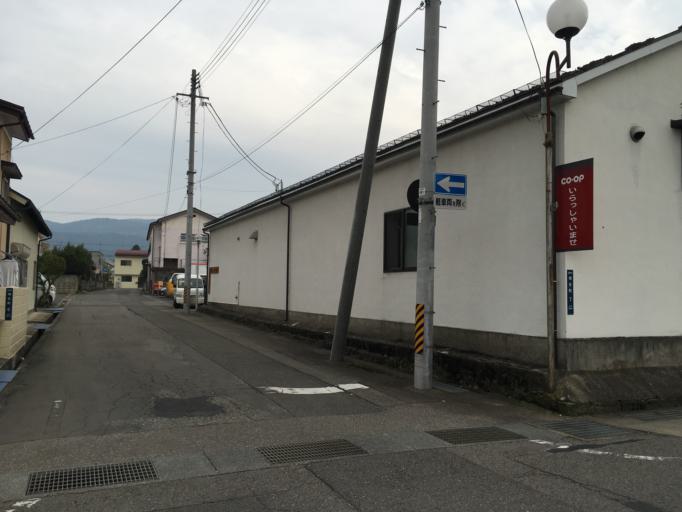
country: JP
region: Fukushima
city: Kitakata
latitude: 37.5017
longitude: 139.9360
